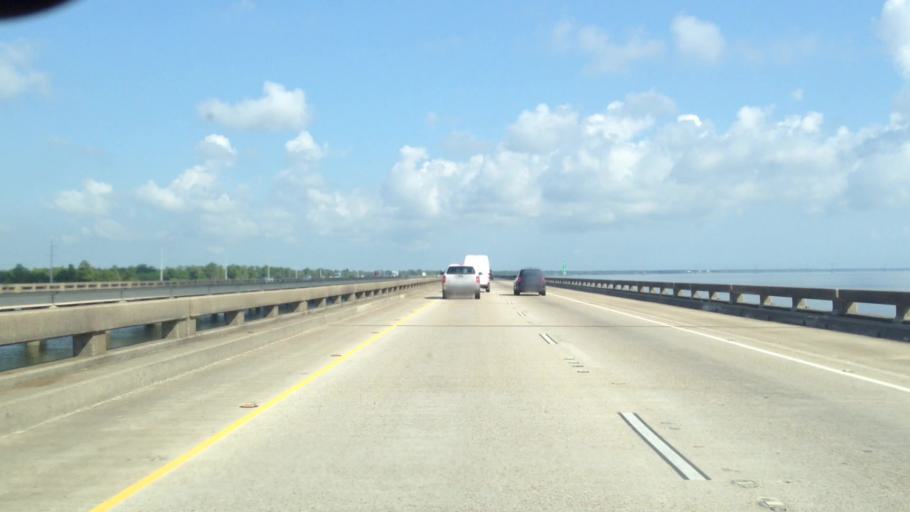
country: US
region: Louisiana
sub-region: Saint Charles Parish
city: Norco
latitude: 30.0620
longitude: -90.3809
